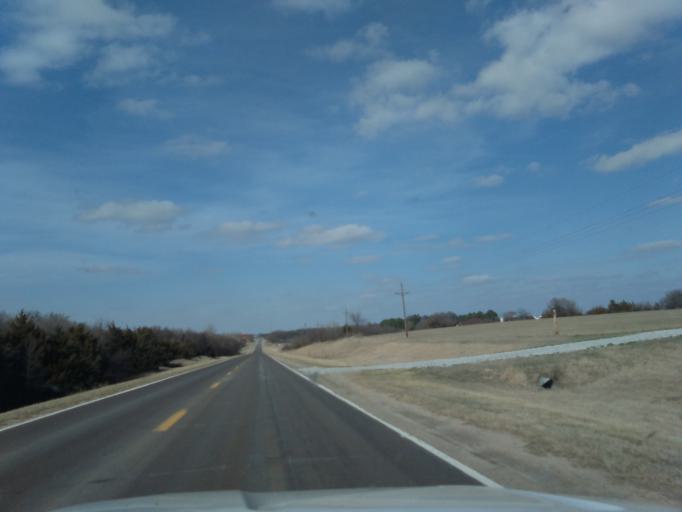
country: US
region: Nebraska
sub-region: Jefferson County
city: Fairbury
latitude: 40.0965
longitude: -96.9351
